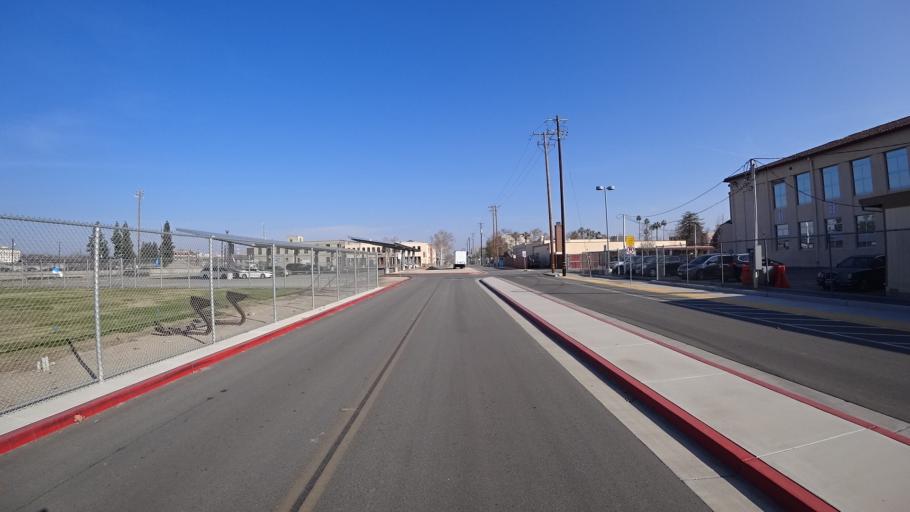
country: US
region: California
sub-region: Kern County
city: Bakersfield
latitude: 35.3705
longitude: -119.0251
